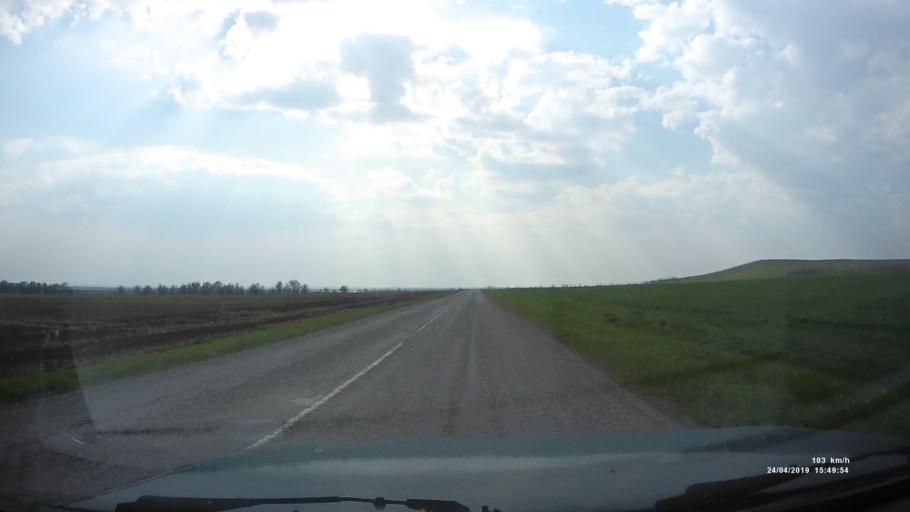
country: RU
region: Kalmykiya
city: Yashalta
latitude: 46.6040
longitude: 42.6447
